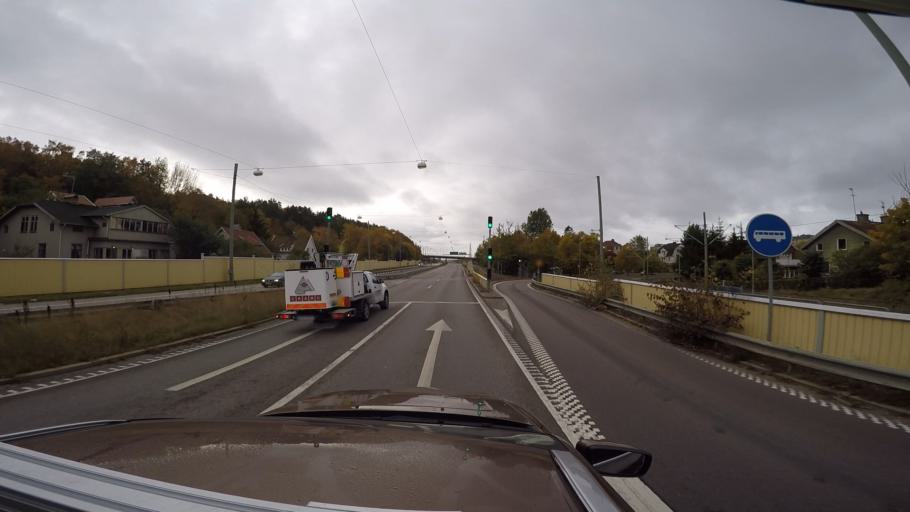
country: SE
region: Vaestra Goetaland
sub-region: Goteborg
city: Majorna
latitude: 57.6755
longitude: 11.9397
